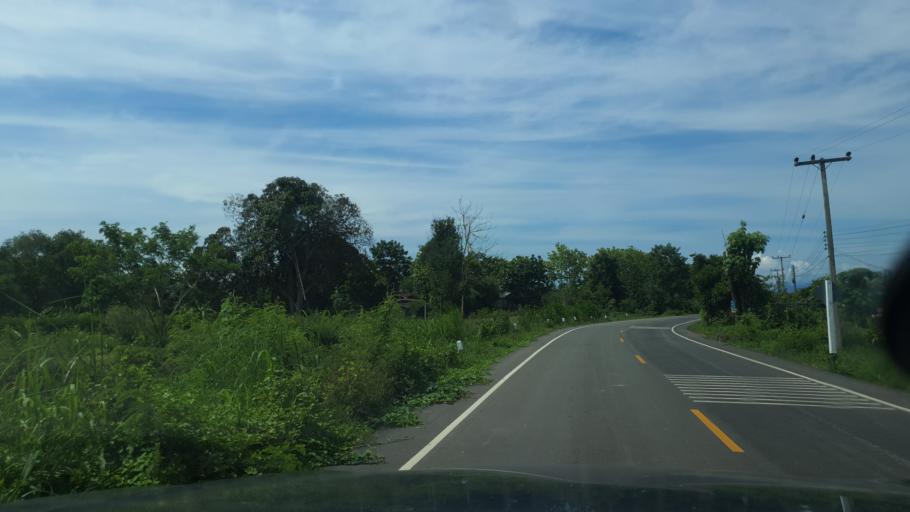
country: TH
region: Sukhothai
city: Si Samrong
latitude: 17.1878
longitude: 99.7376
